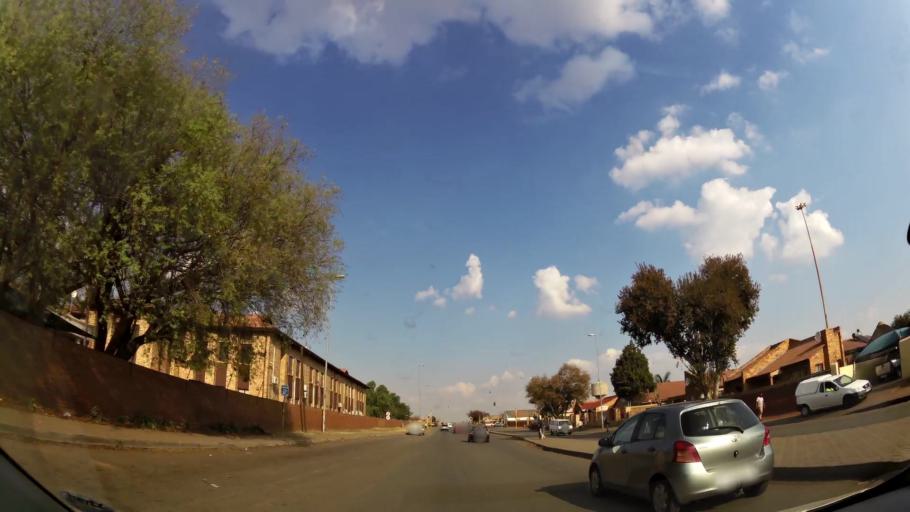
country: ZA
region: Gauteng
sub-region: Ekurhuleni Metropolitan Municipality
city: Germiston
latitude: -26.3444
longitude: 28.2171
